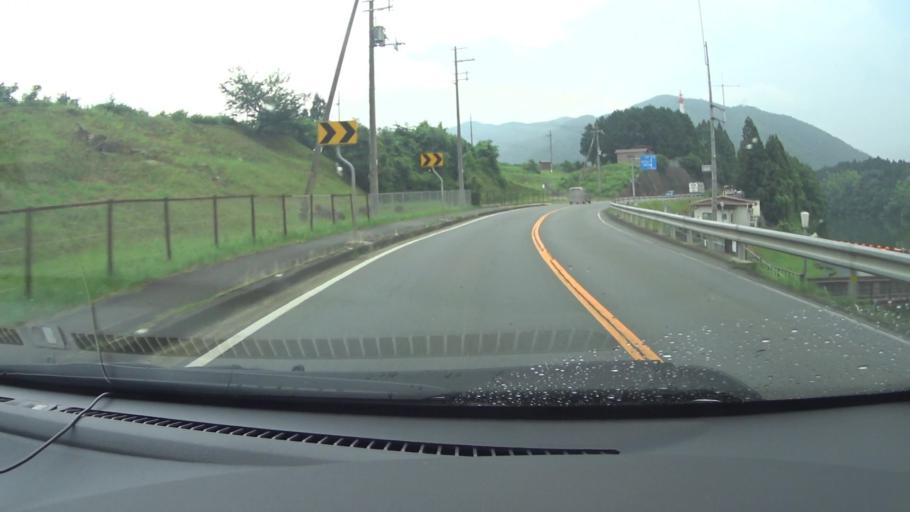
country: JP
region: Kyoto
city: Ayabe
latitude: 35.2524
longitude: 135.4174
